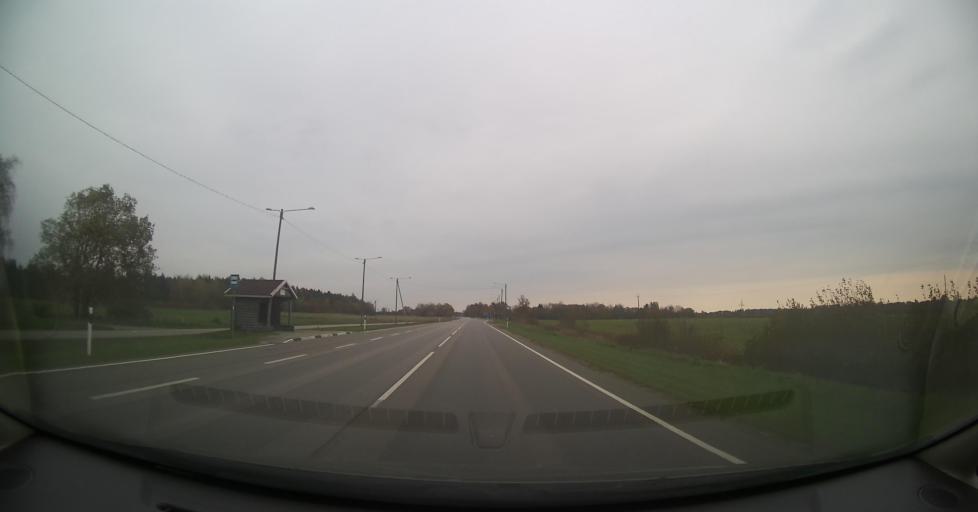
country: EE
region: Laeaene
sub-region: Ridala Parish
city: Uuemoisa
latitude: 58.9565
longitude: 23.7700
